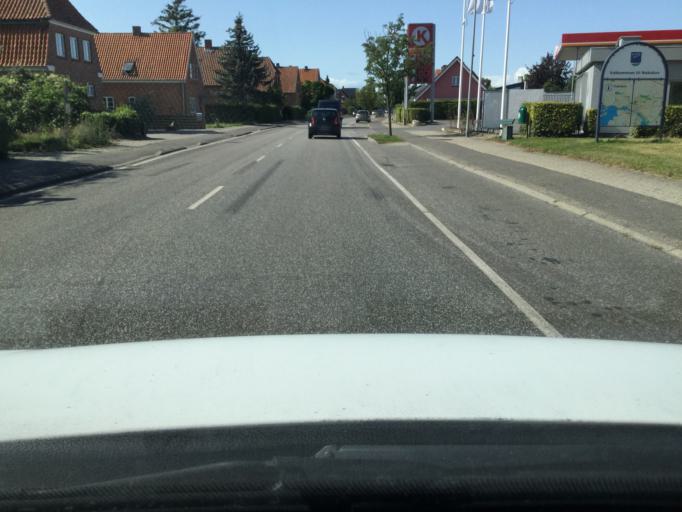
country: DK
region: Zealand
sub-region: Lolland Kommune
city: Nakskov
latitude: 54.8236
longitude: 11.1522
